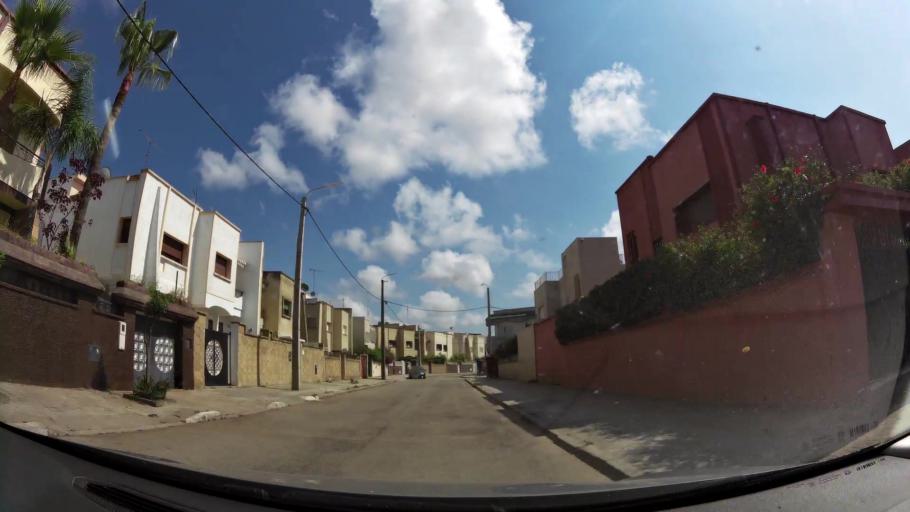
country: MA
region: Rabat-Sale-Zemmour-Zaer
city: Sale
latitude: 34.0376
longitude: -6.7866
